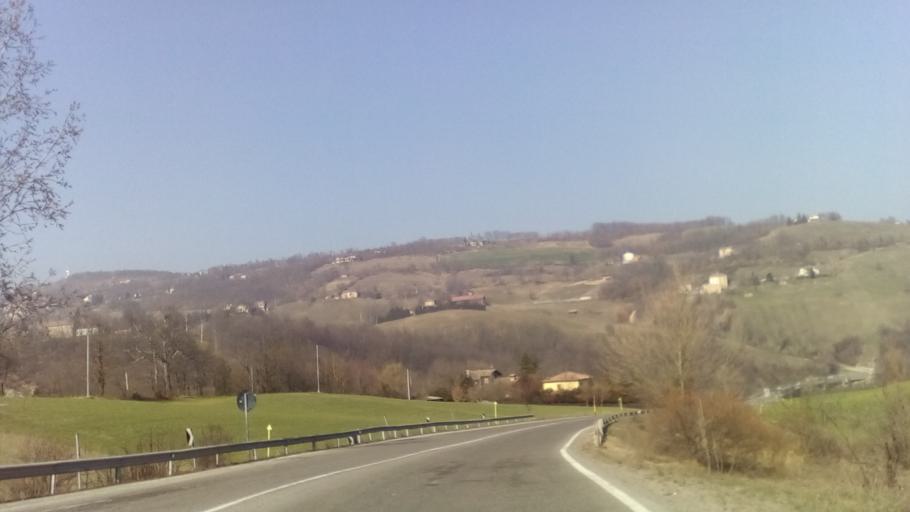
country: IT
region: Emilia-Romagna
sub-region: Provincia di Modena
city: Sant'Antonio
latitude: 44.3998
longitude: 10.8212
